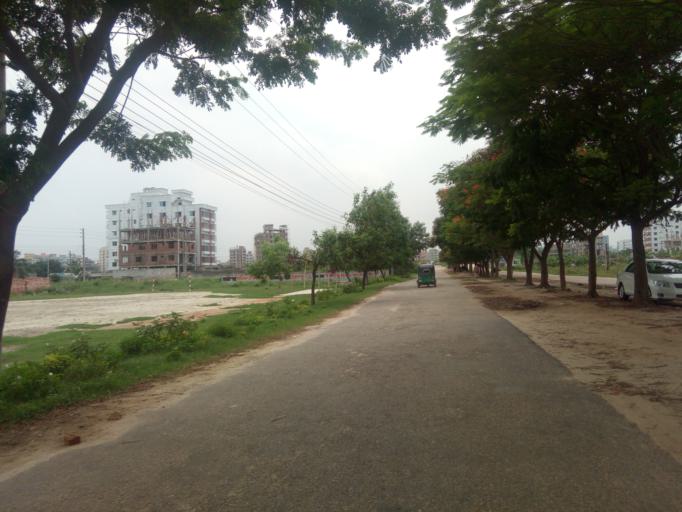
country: BD
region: Dhaka
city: Paltan
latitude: 23.7654
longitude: 90.4402
